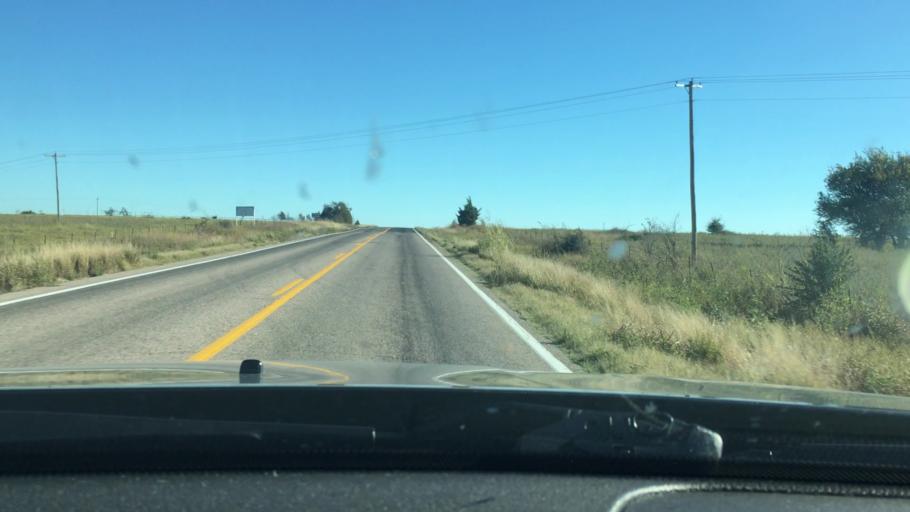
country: US
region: Oklahoma
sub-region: Marshall County
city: Madill
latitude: 34.1058
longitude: -96.7493
